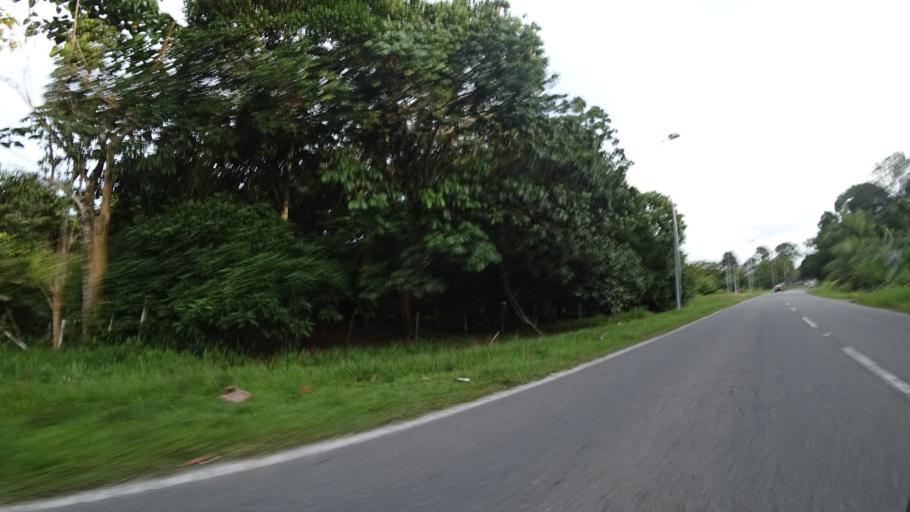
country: BN
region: Brunei and Muara
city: Bandar Seri Begawan
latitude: 4.8530
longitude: 114.8218
